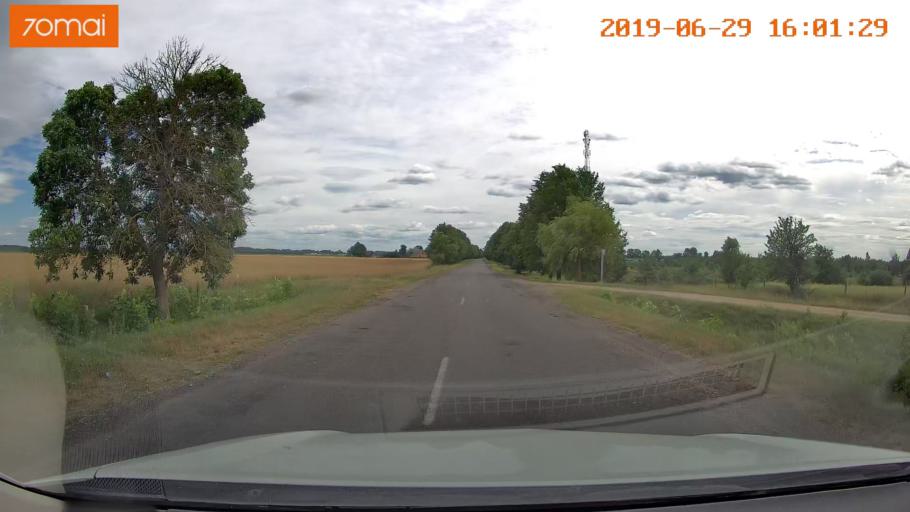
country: BY
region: Brest
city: Luninyets
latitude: 52.2467
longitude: 27.0165
